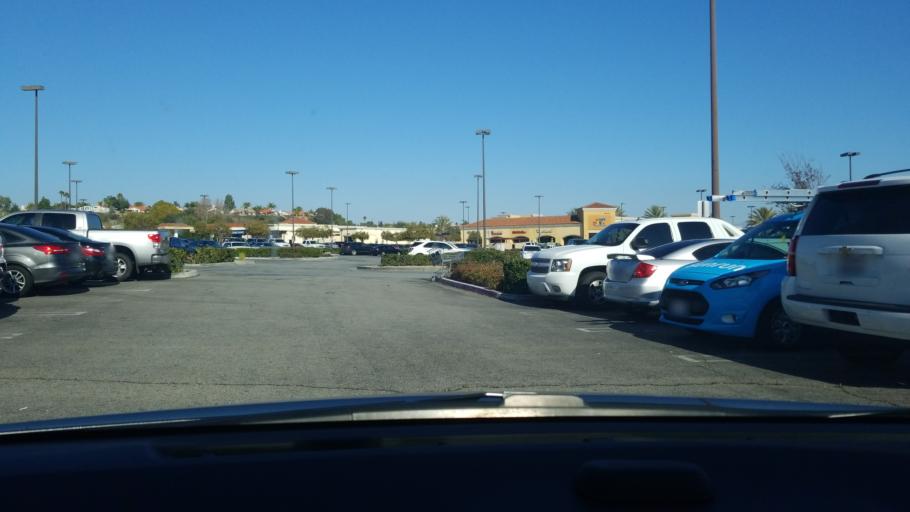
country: US
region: California
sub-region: Riverside County
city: Murrieta Hot Springs
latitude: 33.5544
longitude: -117.1791
